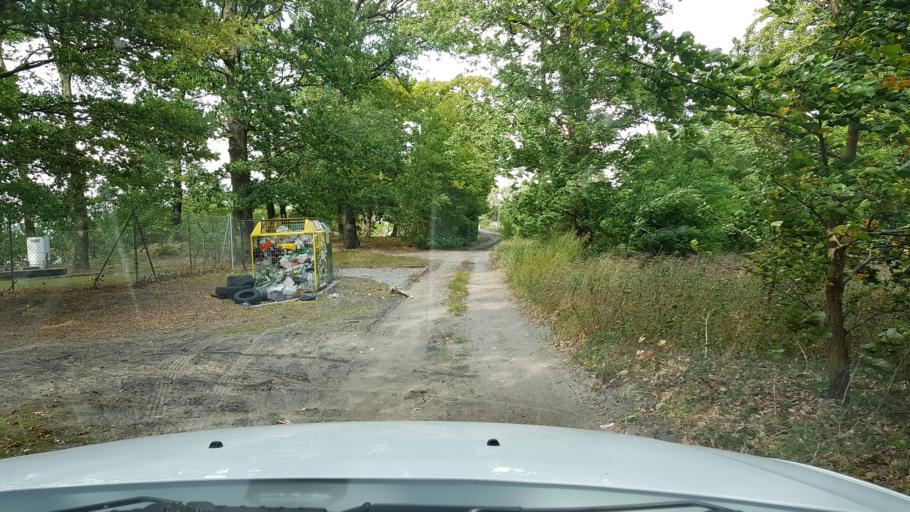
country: PL
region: West Pomeranian Voivodeship
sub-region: Powiat gryfinski
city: Gryfino
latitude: 53.3036
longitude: 14.5071
